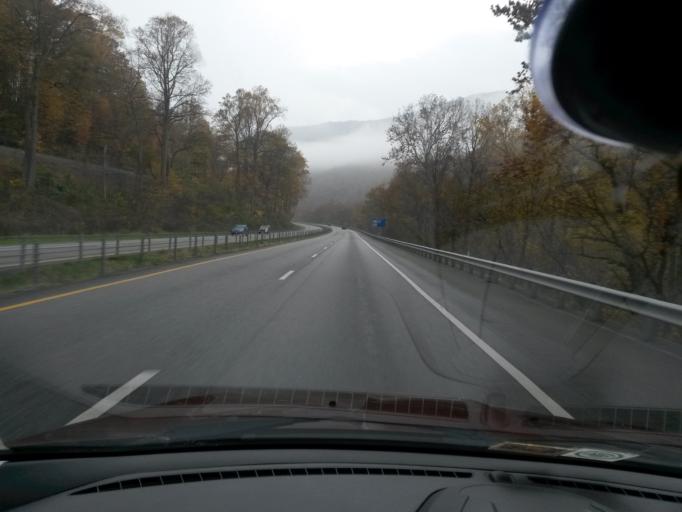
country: US
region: Virginia
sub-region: City of Covington
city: Fairlawn
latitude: 37.7786
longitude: -79.9210
